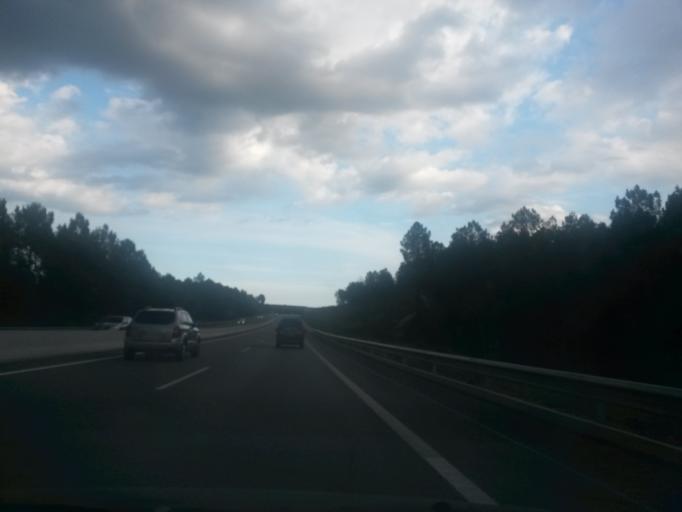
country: ES
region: Catalonia
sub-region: Provincia de Girona
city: Brunyola
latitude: 41.8900
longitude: 2.6684
